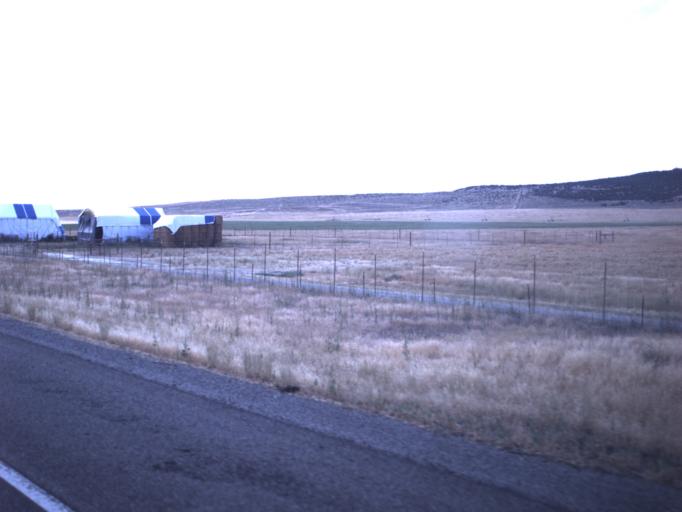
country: US
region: Idaho
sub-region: Oneida County
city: Malad City
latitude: 41.9768
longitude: -112.7923
